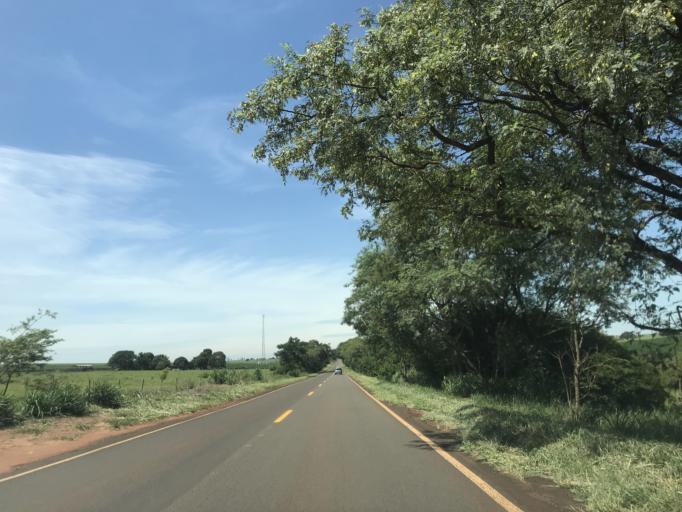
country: BR
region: Parana
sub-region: Paranavai
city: Nova Aurora
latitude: -22.8139
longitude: -52.6545
